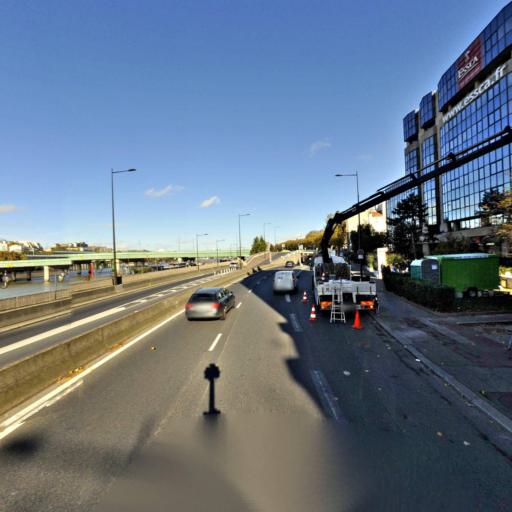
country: FR
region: Ile-de-France
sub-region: Departement des Hauts-de-Seine
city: Sevres
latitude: 48.8399
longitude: 2.2244
